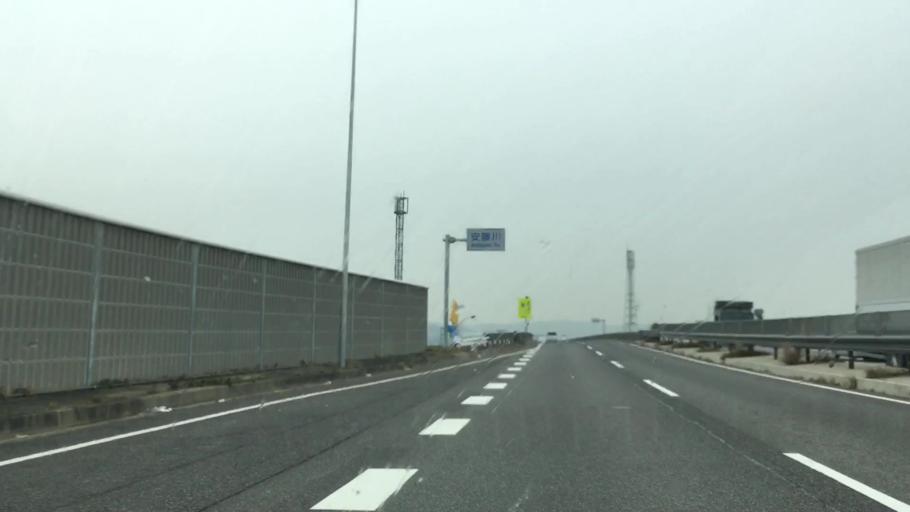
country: JP
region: Aichi
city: Nishio
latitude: 34.8742
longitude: 137.0823
